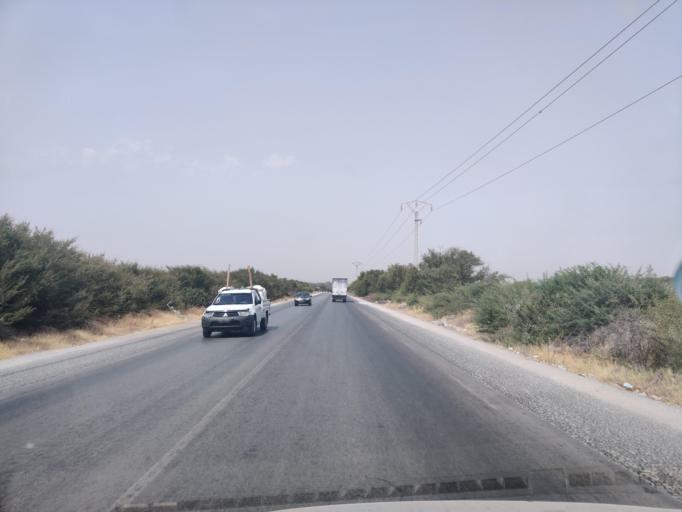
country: TN
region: Tunis
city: La Sebala du Mornag
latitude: 36.6496
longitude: 10.3425
